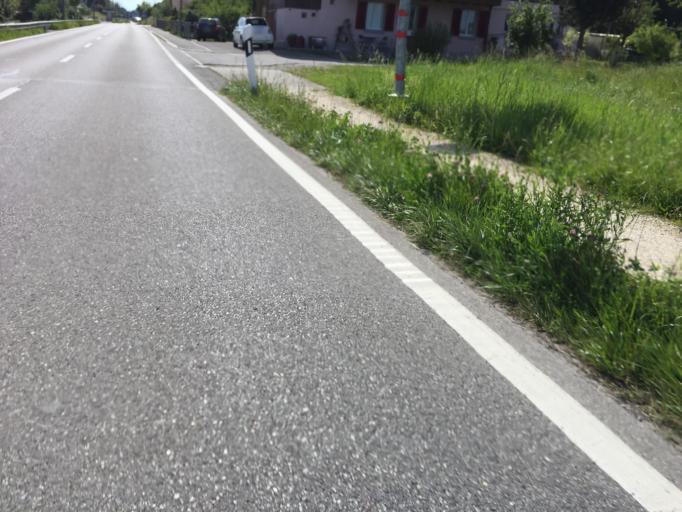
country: CH
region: Bern
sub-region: Bern-Mittelland District
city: Stettlen
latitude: 46.9312
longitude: 7.5239
